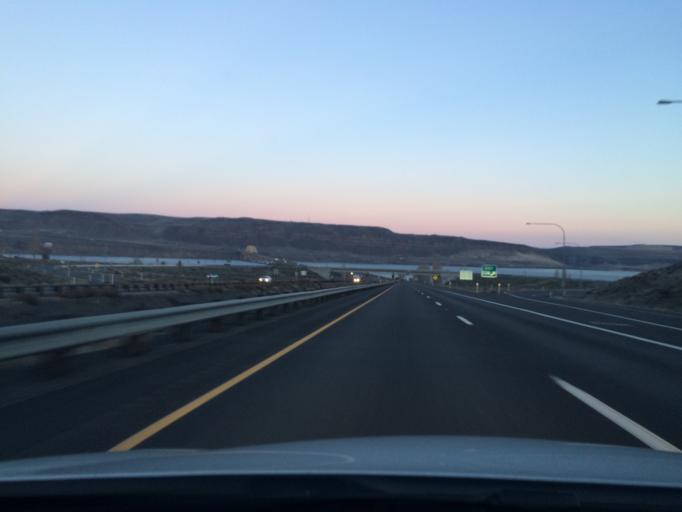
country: US
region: Washington
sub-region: Grant County
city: Mattawa
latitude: 46.9404
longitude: -119.9943
